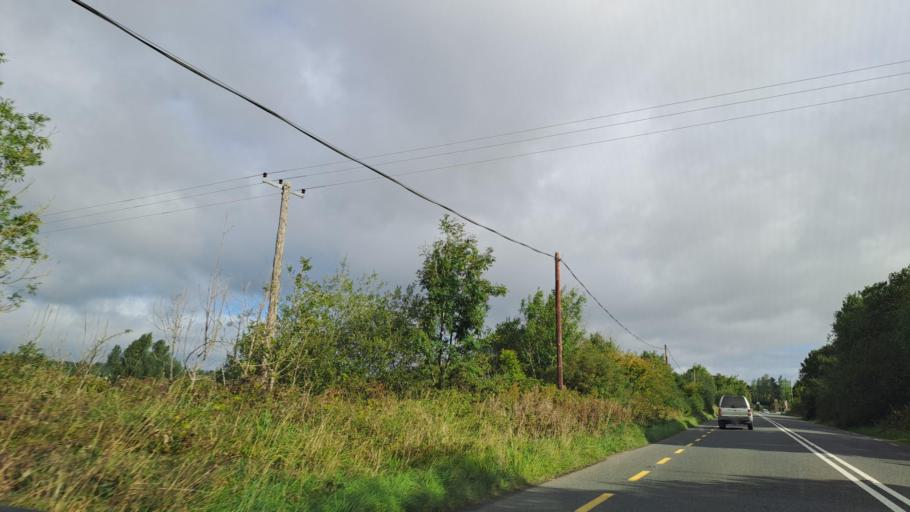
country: IE
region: Ulster
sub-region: County Monaghan
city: Carrickmacross
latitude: 53.9478
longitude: -6.7634
